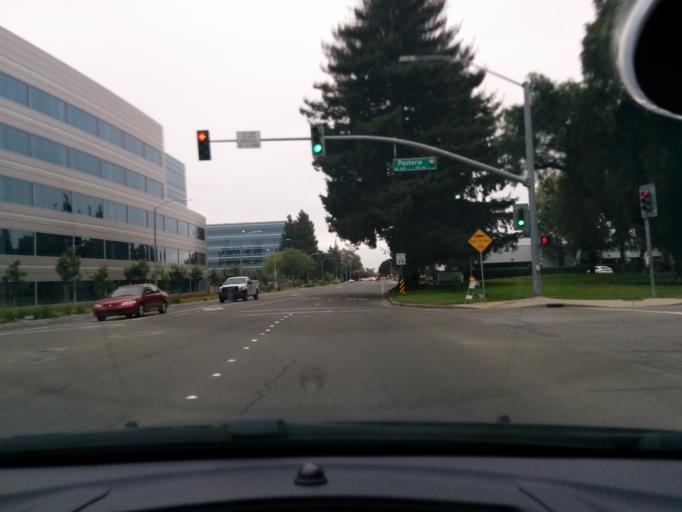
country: US
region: California
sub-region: Santa Clara County
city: Sunnyvale
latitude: 37.3909
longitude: -122.0343
